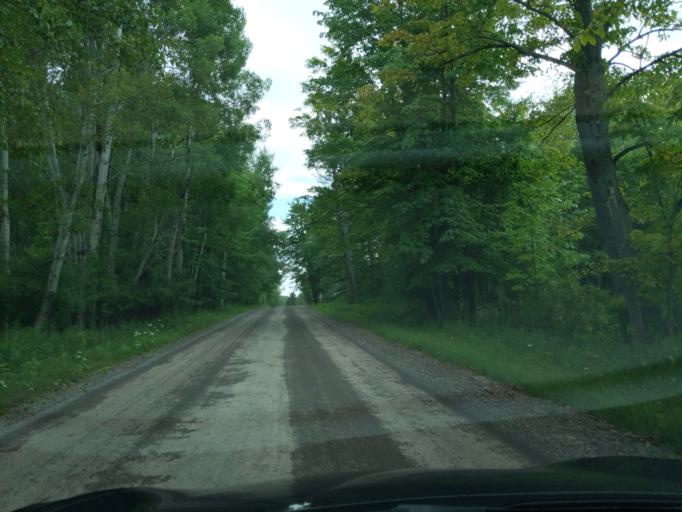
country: US
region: Michigan
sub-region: Clare County
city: Harrison
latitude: 43.9804
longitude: -84.9983
